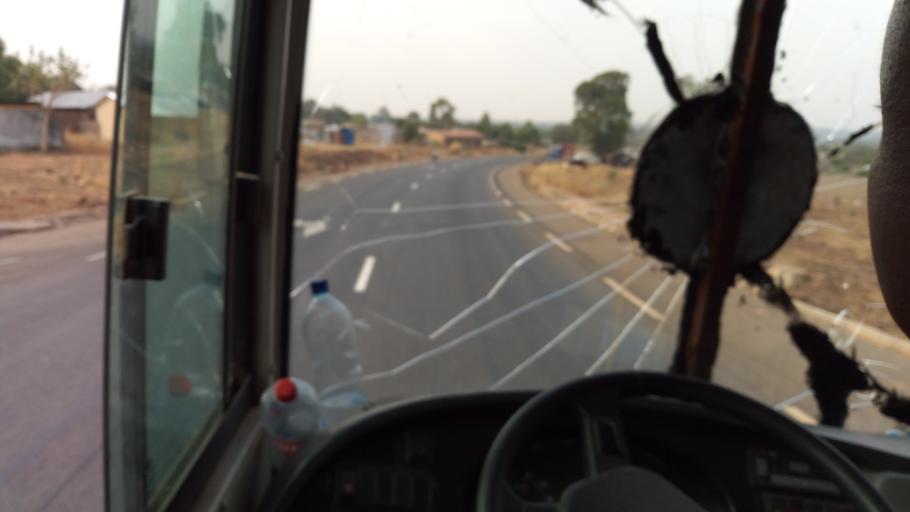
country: TG
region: Kara
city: Bafilo
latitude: 9.3548
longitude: 1.2602
